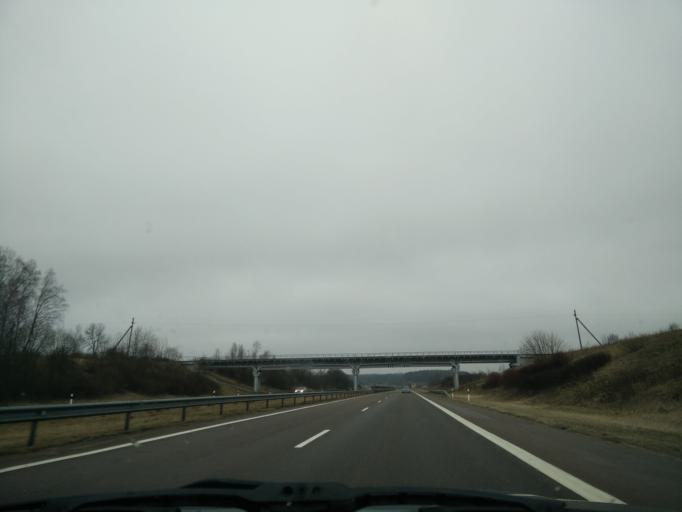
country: LT
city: Skaudvile
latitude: 55.4071
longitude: 22.8401
